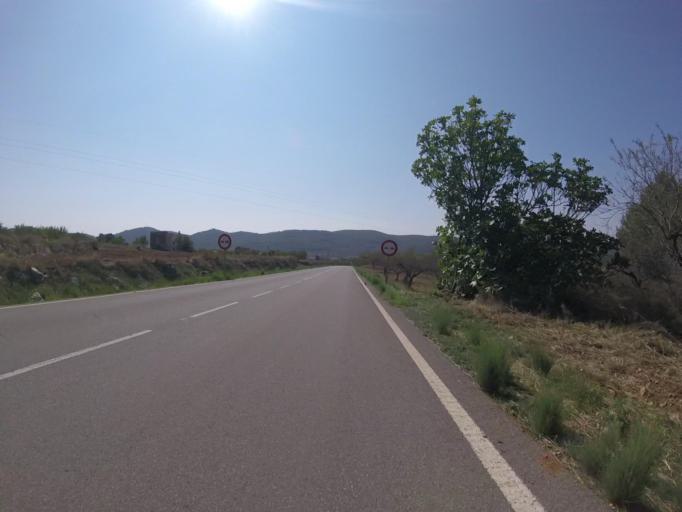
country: ES
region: Valencia
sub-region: Provincia de Castello
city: Adzaneta
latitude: 40.2286
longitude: -0.1750
